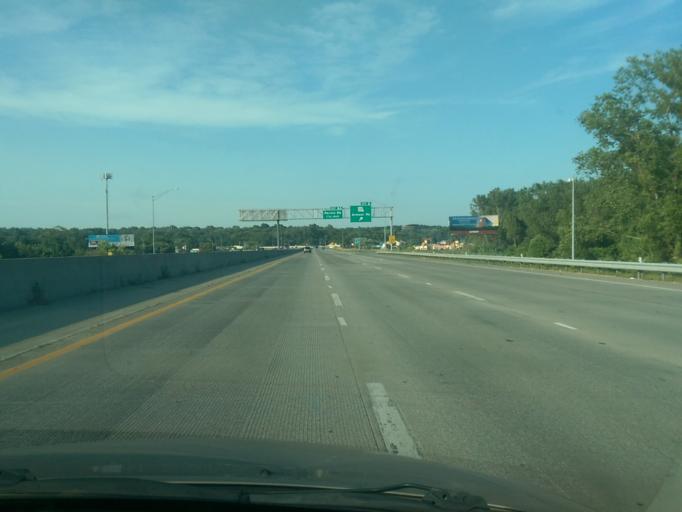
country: US
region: Missouri
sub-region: Clay County
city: North Kansas City
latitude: 39.1409
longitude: -94.5650
